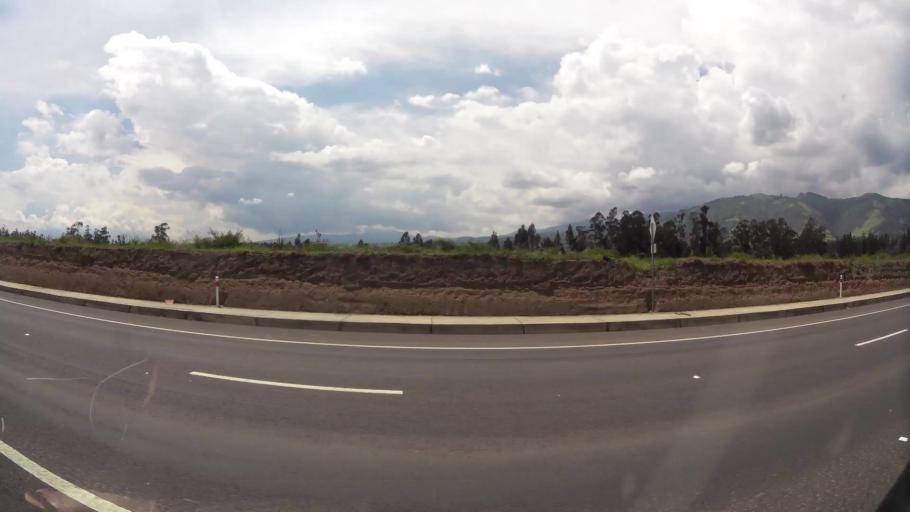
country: EC
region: Pichincha
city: Sangolqui
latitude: -0.1974
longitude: -78.3381
